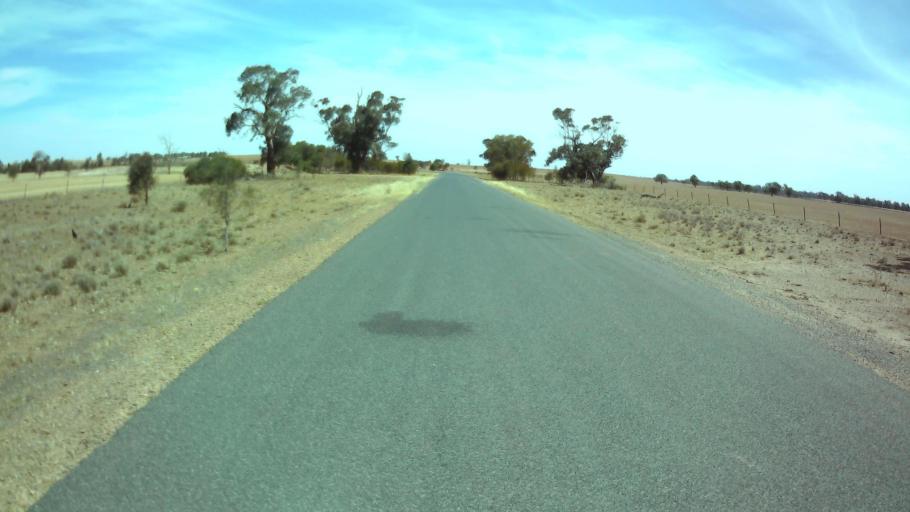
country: AU
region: New South Wales
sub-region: Weddin
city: Grenfell
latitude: -33.8851
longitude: 147.7421
